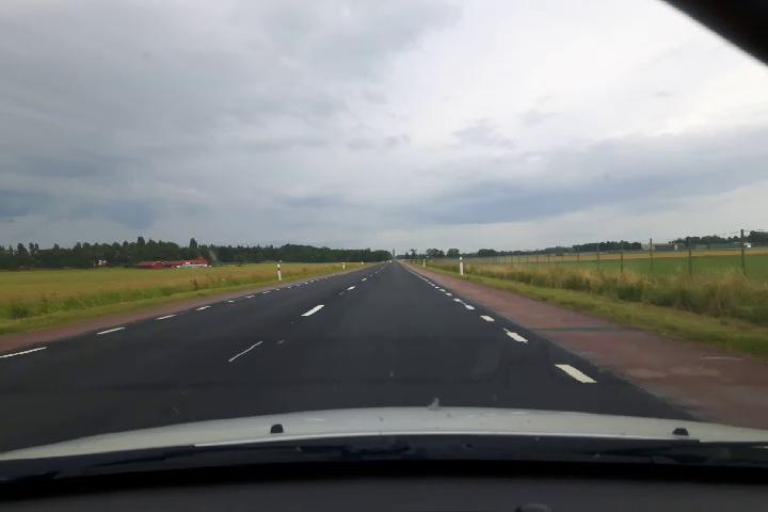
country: SE
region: Uppsala
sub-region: Uppsala Kommun
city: Gamla Uppsala
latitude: 59.8957
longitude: 17.6145
